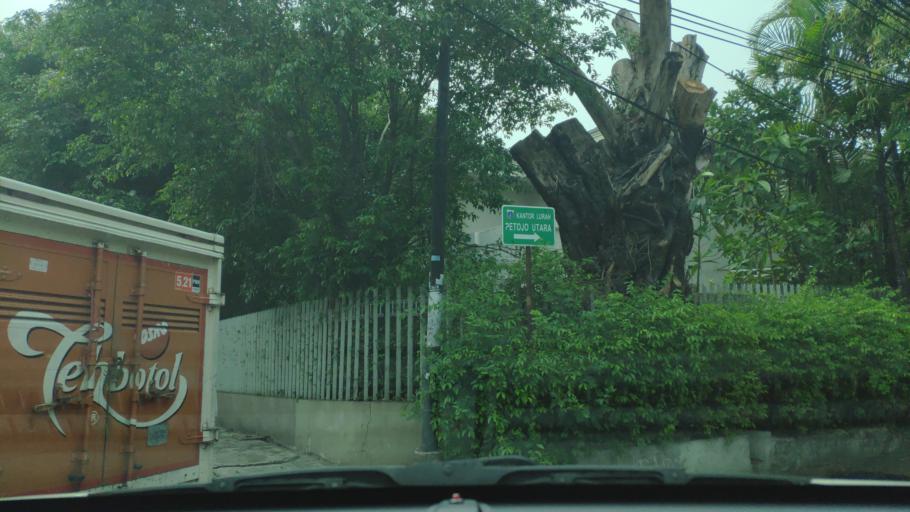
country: ID
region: Jakarta Raya
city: Jakarta
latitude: -6.1640
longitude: 106.8168
